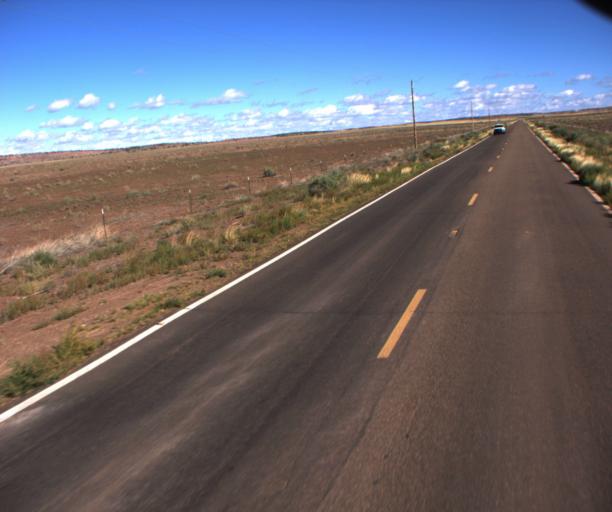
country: US
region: Arizona
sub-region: Apache County
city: Saint Johns
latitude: 34.6184
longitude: -109.3169
